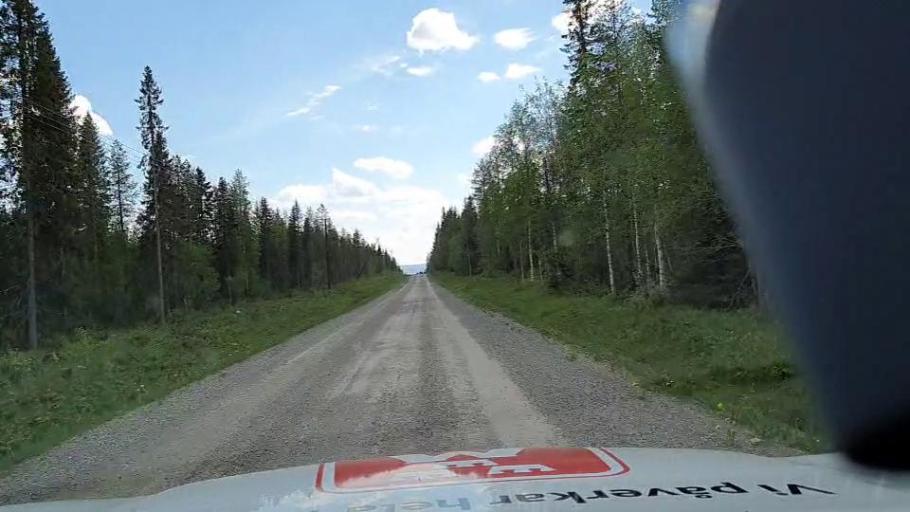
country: SE
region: Jaemtland
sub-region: Stroemsunds Kommun
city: Stroemsund
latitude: 64.5268
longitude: 15.5914
